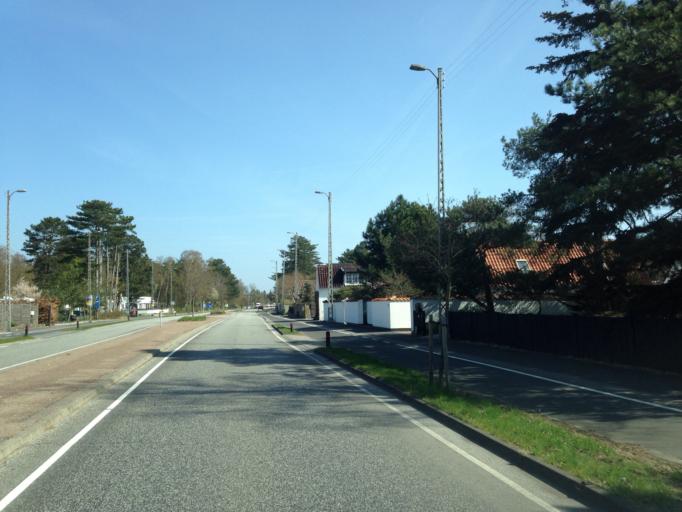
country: DK
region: Zealand
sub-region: Greve Kommune
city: Greve
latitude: 55.5758
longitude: 12.2960
